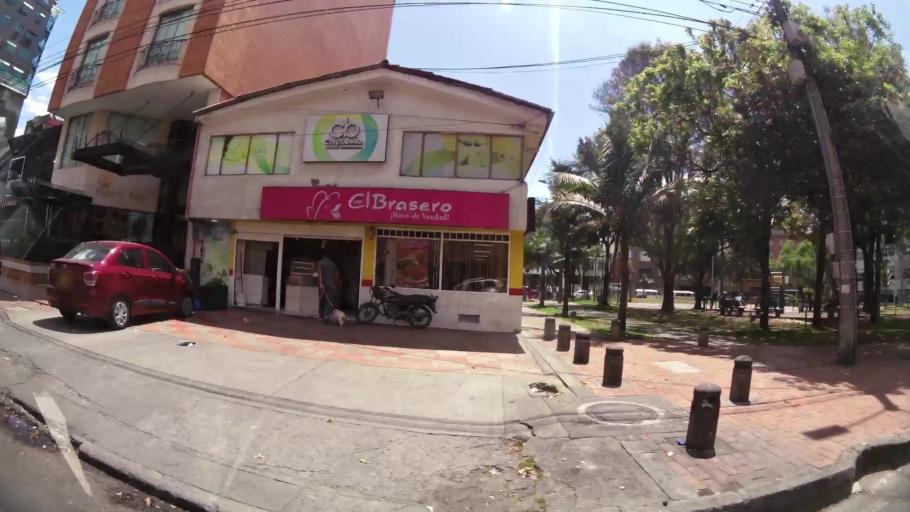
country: CO
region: Bogota D.C.
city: Bogota
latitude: 4.6342
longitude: -74.0952
